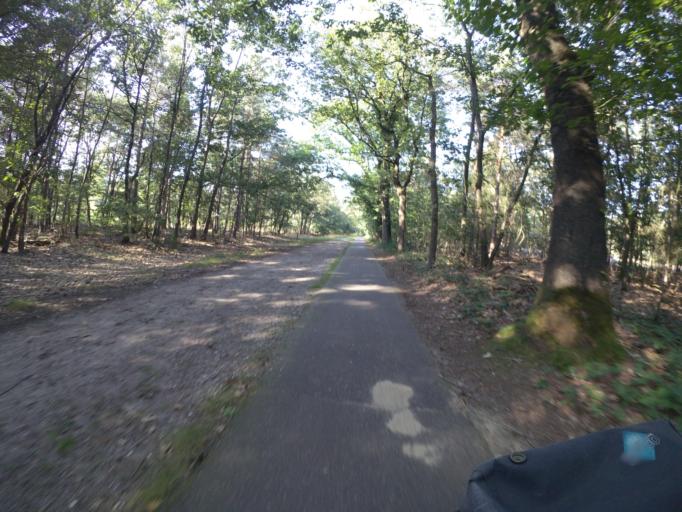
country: NL
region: North Brabant
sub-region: Gemeente Landerd
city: Schaijk
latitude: 51.7186
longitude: 5.6288
